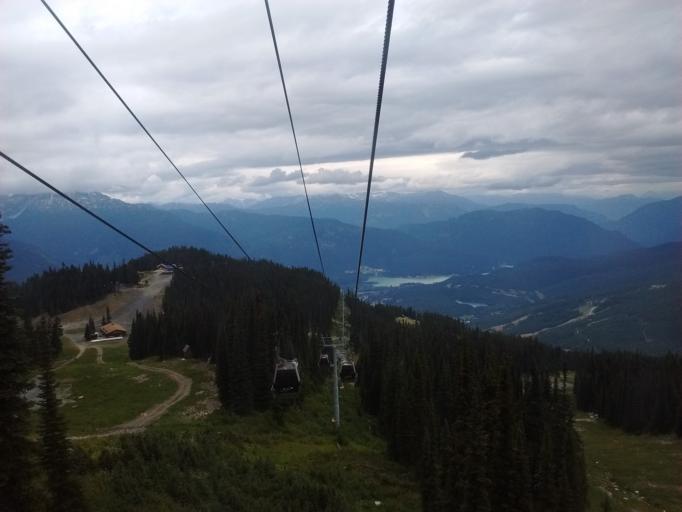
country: CA
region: British Columbia
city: Whistler
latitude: 50.0733
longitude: -122.9476
